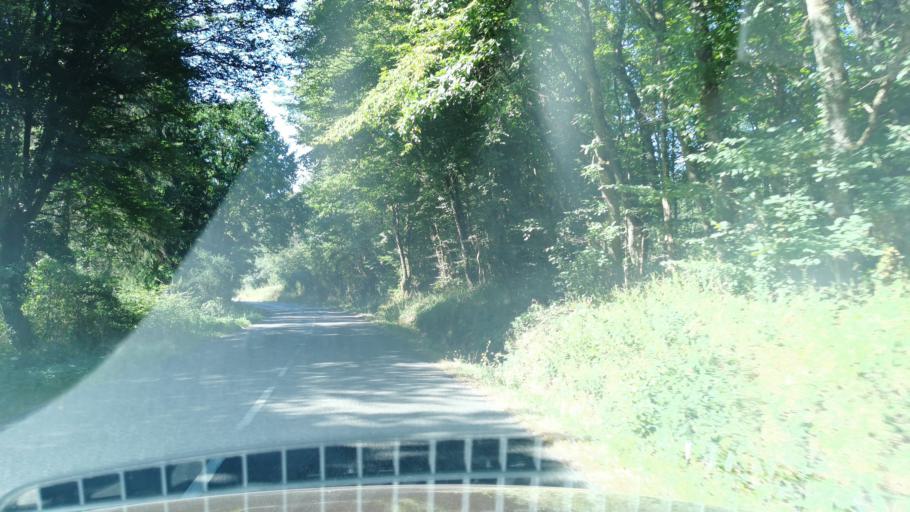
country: FR
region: Bourgogne
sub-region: Departement de Saone-et-Loire
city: Torcy
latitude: 46.7741
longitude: 4.4719
